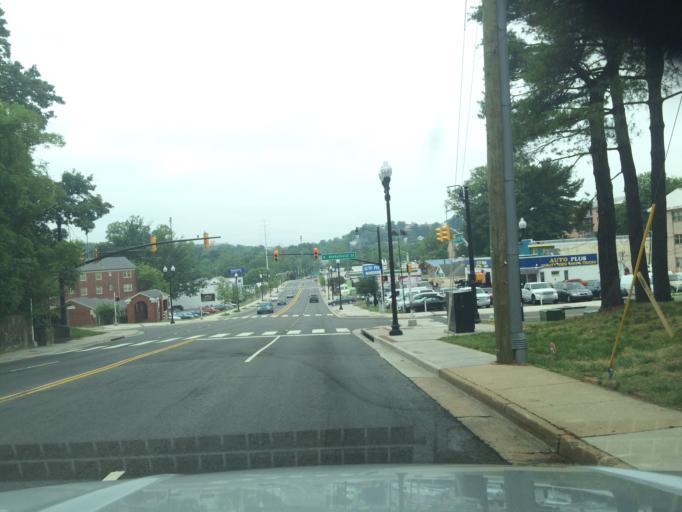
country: US
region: Virginia
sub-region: Arlington County
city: Arlington
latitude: 38.8575
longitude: -77.1060
